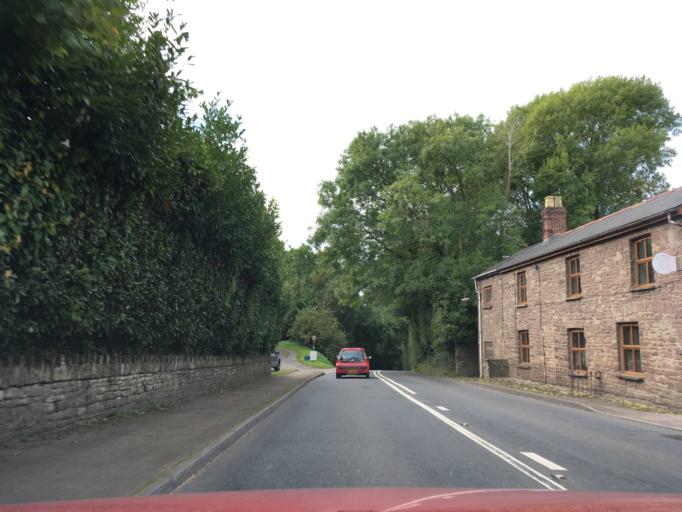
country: GB
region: England
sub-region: Gloucestershire
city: Bream
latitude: 51.7035
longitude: -2.5783
